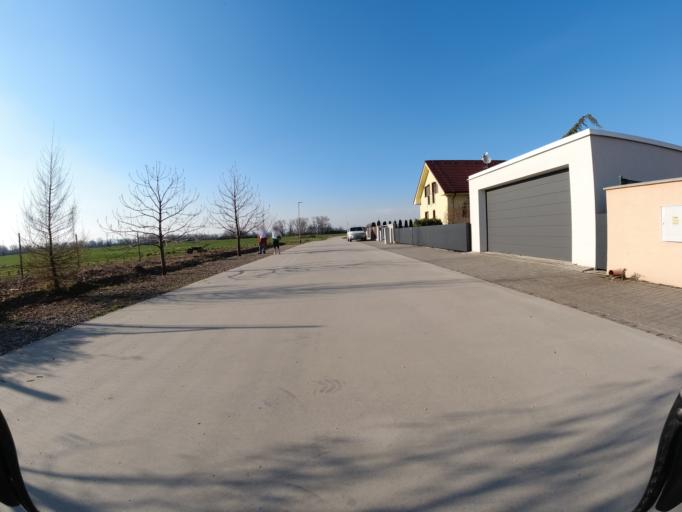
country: SK
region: Trnavsky
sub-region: Okres Trnava
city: Piestany
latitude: 48.6266
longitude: 17.8626
